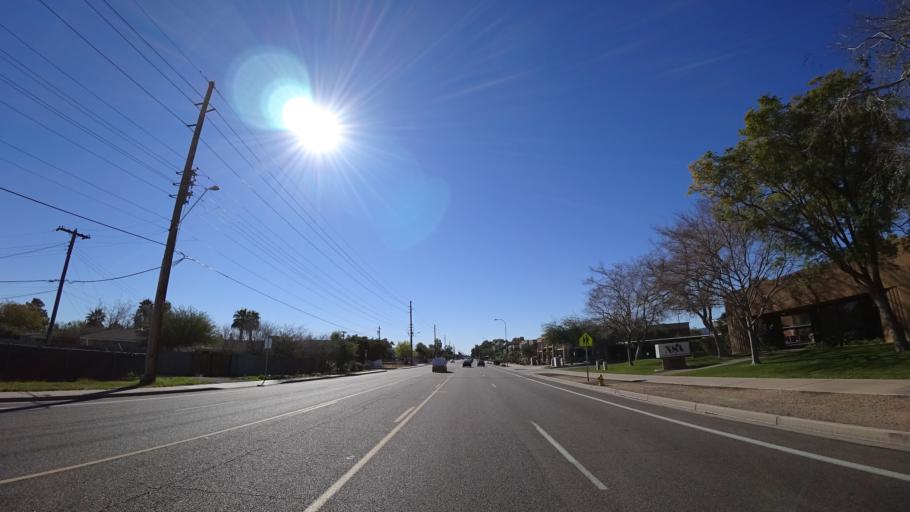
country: US
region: Arizona
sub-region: Maricopa County
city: Tempe Junction
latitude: 33.4122
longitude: -111.9609
